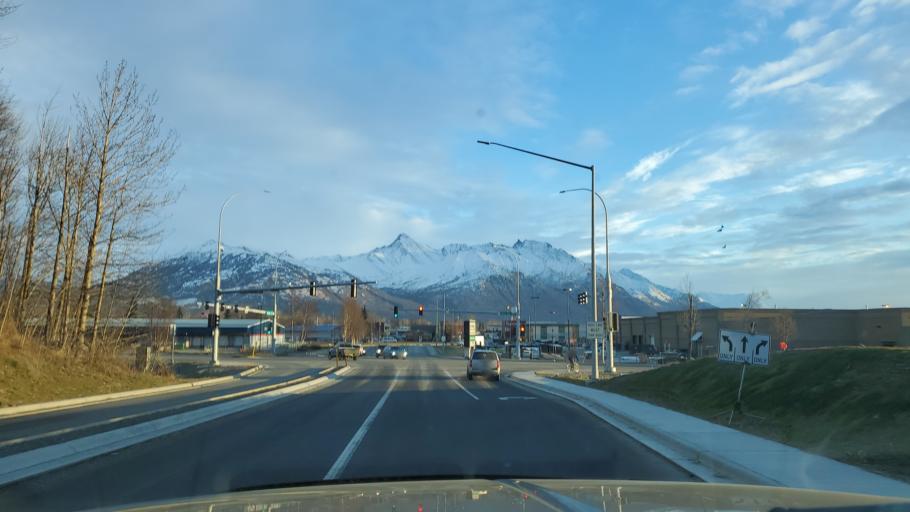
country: US
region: Alaska
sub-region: Matanuska-Susitna Borough
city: Palmer
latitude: 61.6017
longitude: -149.1235
